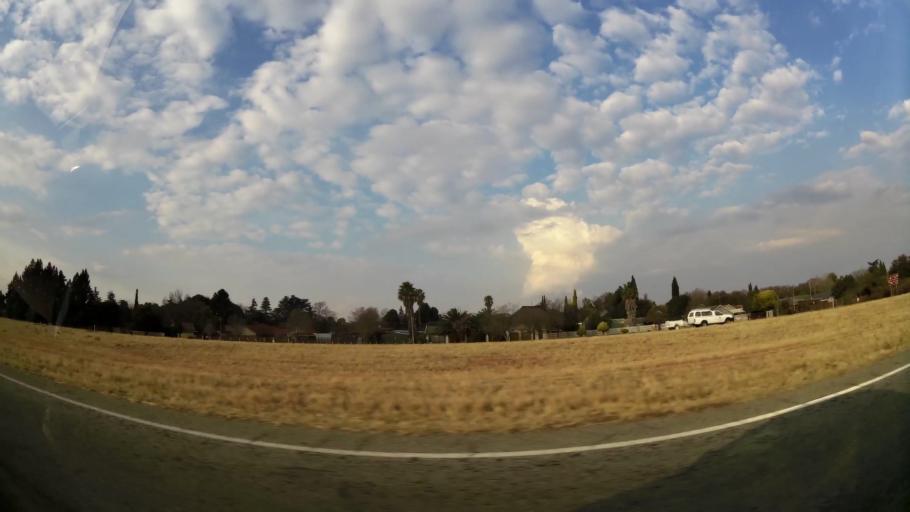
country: ZA
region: Gauteng
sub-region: Sedibeng District Municipality
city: Vanderbijlpark
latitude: -26.7309
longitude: 27.8212
